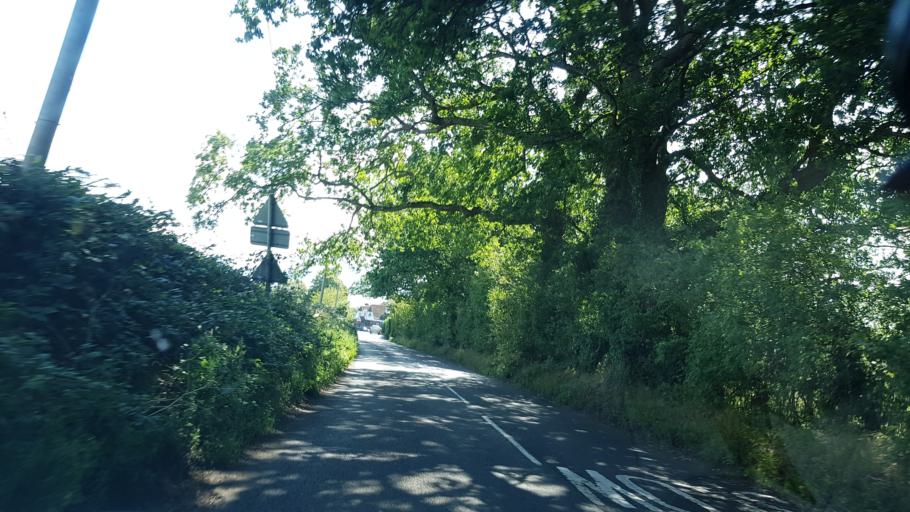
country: GB
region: England
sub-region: Surrey
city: Ripley
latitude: 51.3042
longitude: -0.5096
